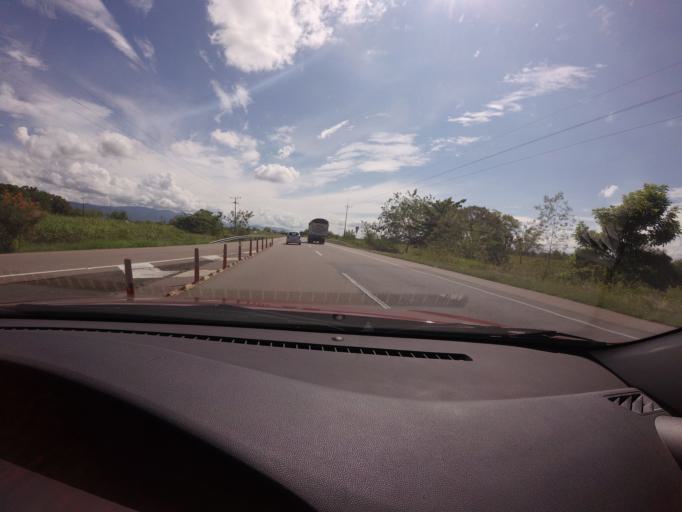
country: CO
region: Cundinamarca
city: Puerto Salgar
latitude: 5.6653
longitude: -74.6142
